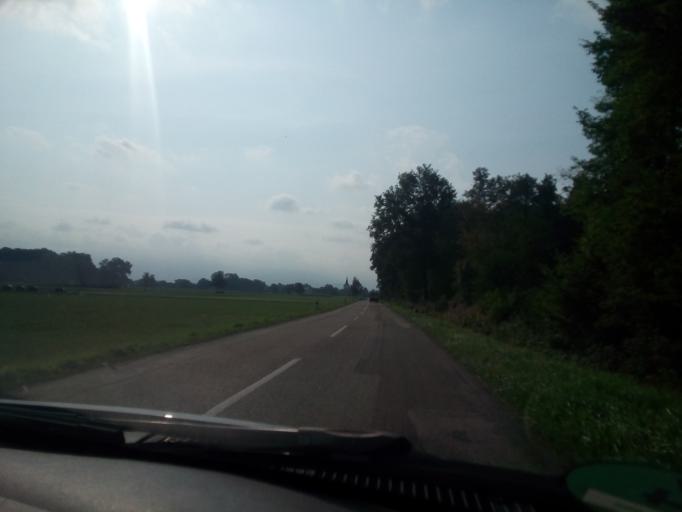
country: DE
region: Baden-Wuerttemberg
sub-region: Karlsruhe Region
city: Lichtenau
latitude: 48.6704
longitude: 8.0061
